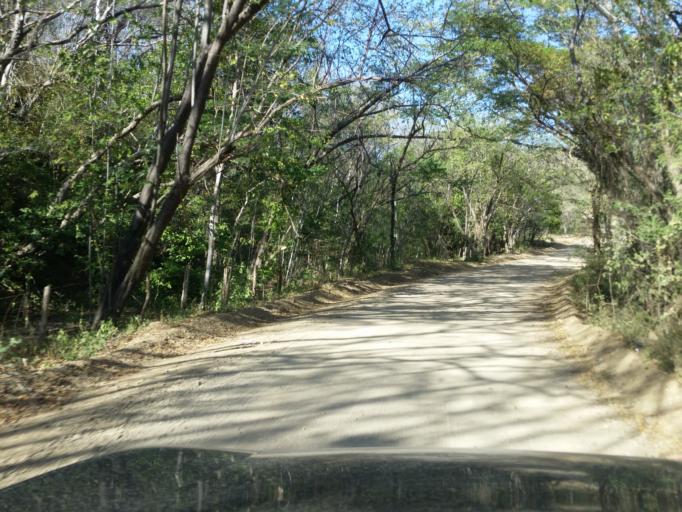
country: NI
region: Rivas
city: San Juan del Sur
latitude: 11.1651
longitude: -85.7985
